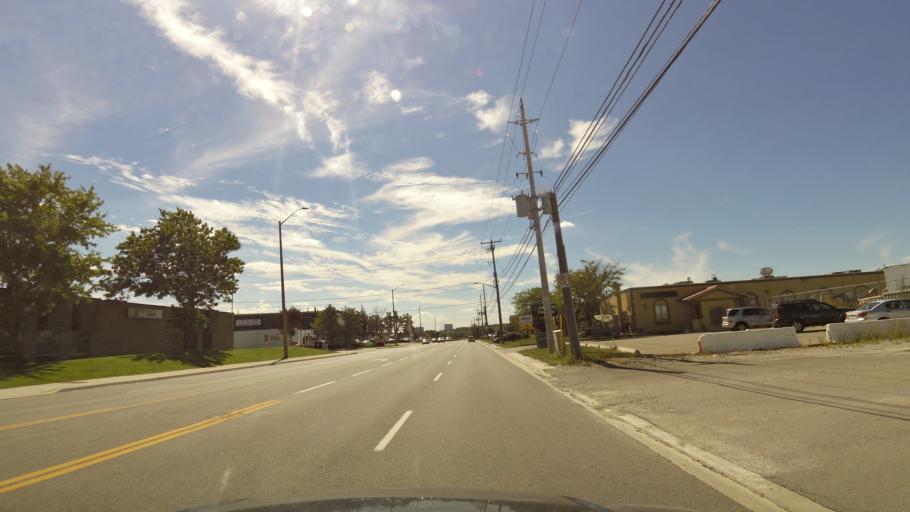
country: CA
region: Ontario
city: Mississauga
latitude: 43.6394
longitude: -79.6338
